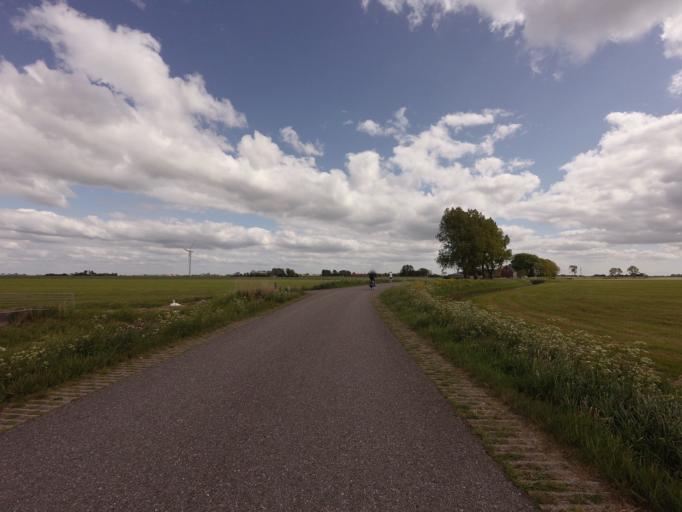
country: NL
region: Friesland
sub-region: Sudwest Fryslan
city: Bolsward
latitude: 53.0817
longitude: 5.5506
